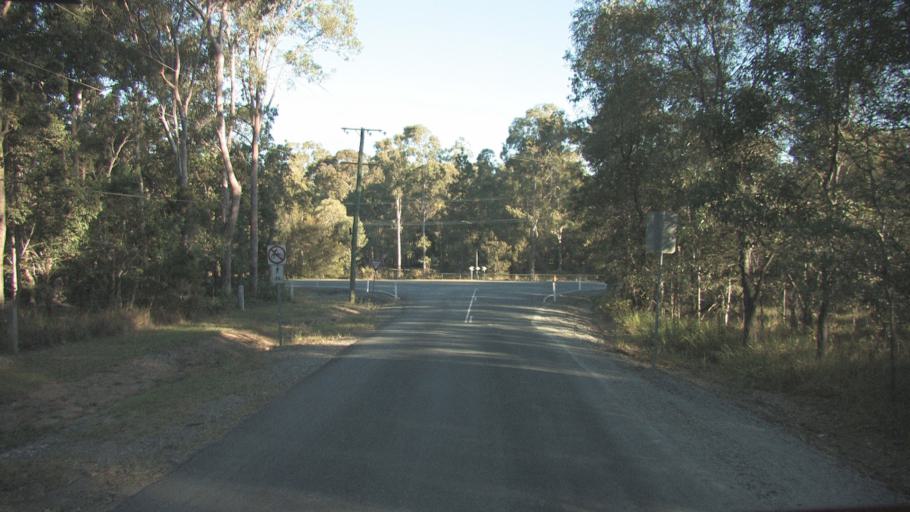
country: AU
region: Queensland
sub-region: Logan
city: Chambers Flat
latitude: -27.7691
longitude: 153.1324
